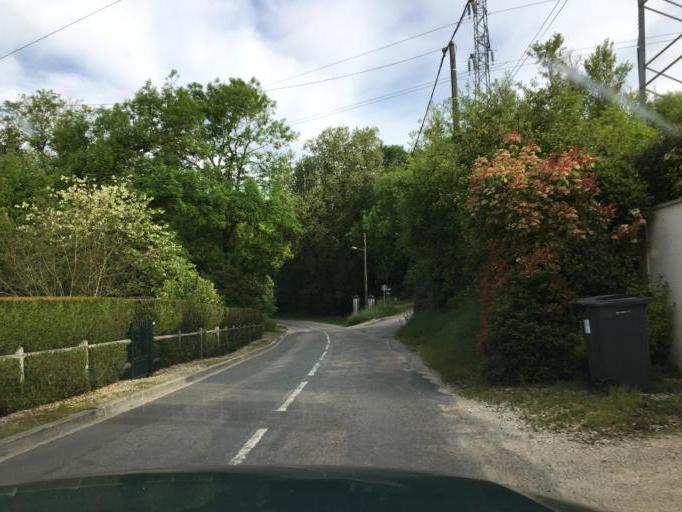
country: FR
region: Centre
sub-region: Departement du Loiret
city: Saint-Ay
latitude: 47.8677
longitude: 1.7449
